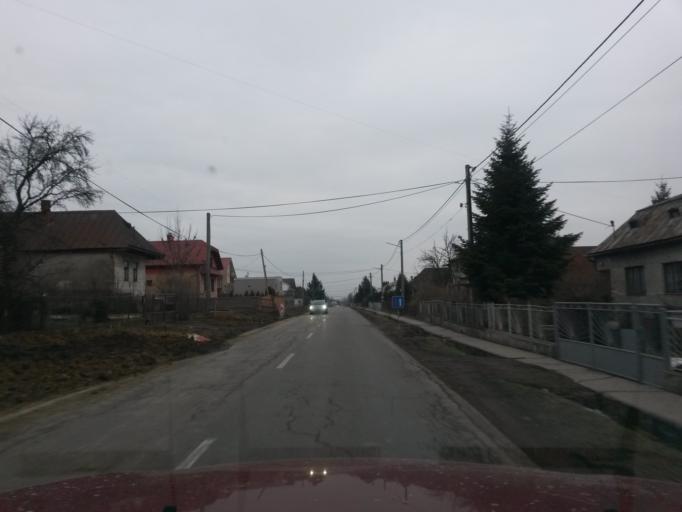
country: SK
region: Kosicky
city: Trebisov
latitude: 48.6966
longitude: 21.8084
